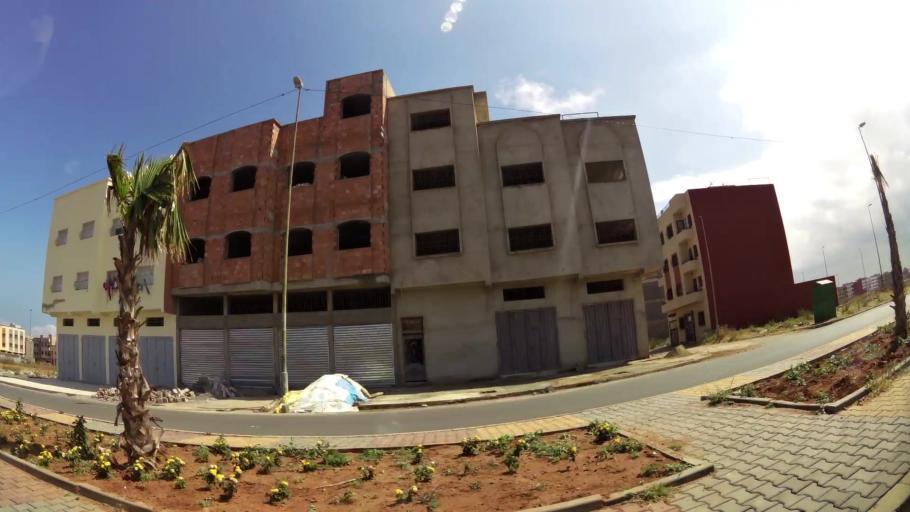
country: MA
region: Rabat-Sale-Zemmour-Zaer
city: Sale
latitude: 34.0747
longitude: -6.7724
